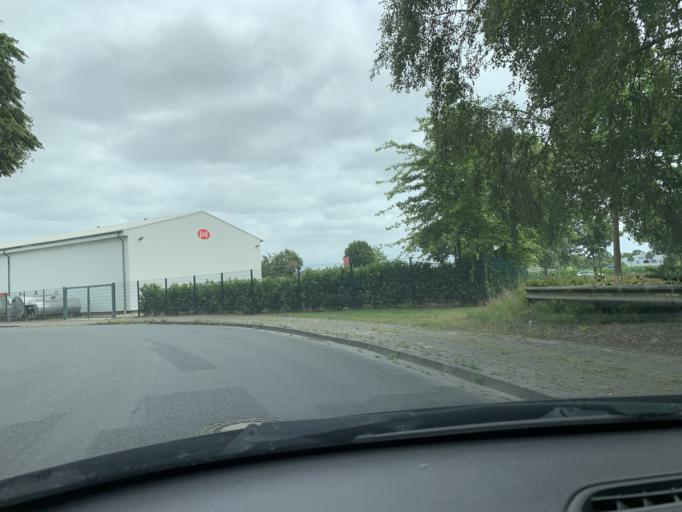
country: DE
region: Lower Saxony
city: Westerstede
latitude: 53.2683
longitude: 7.9469
